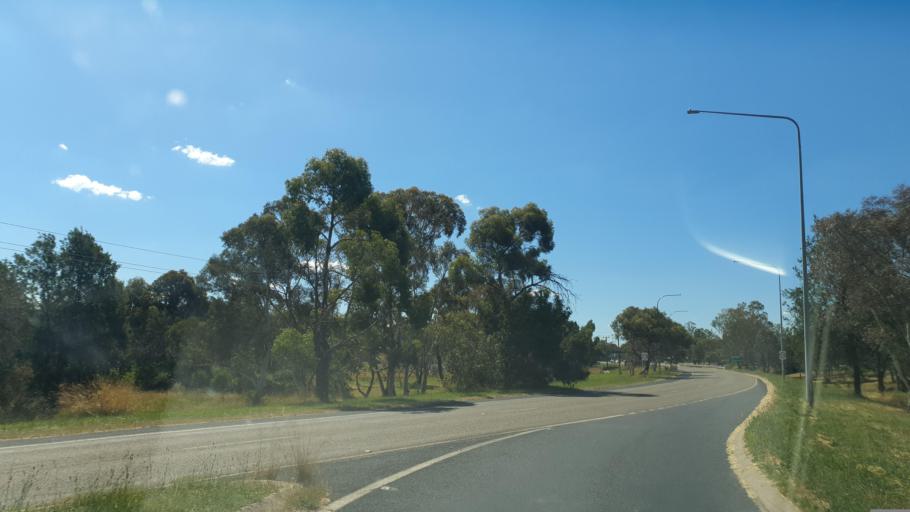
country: AU
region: Australian Capital Territory
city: Belconnen
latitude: -35.2099
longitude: 149.0368
